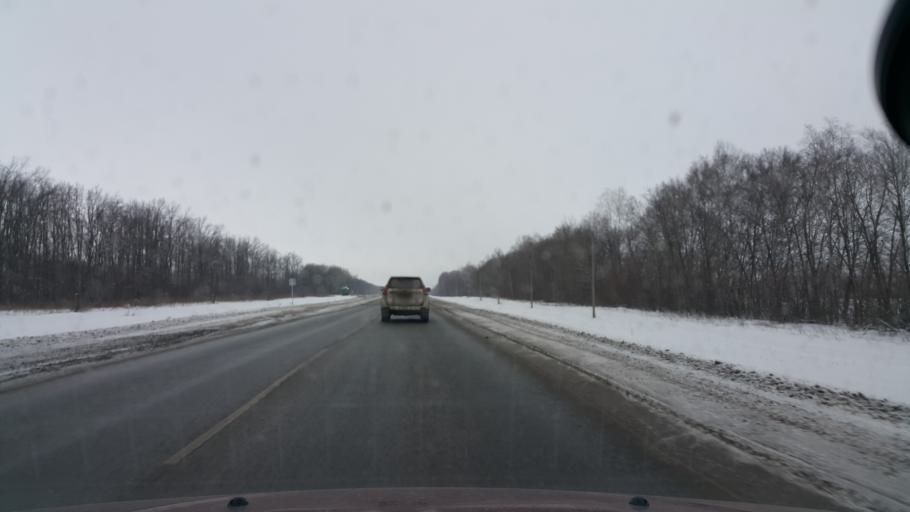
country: RU
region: Tambov
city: Kotovsk
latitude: 52.5841
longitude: 41.4501
